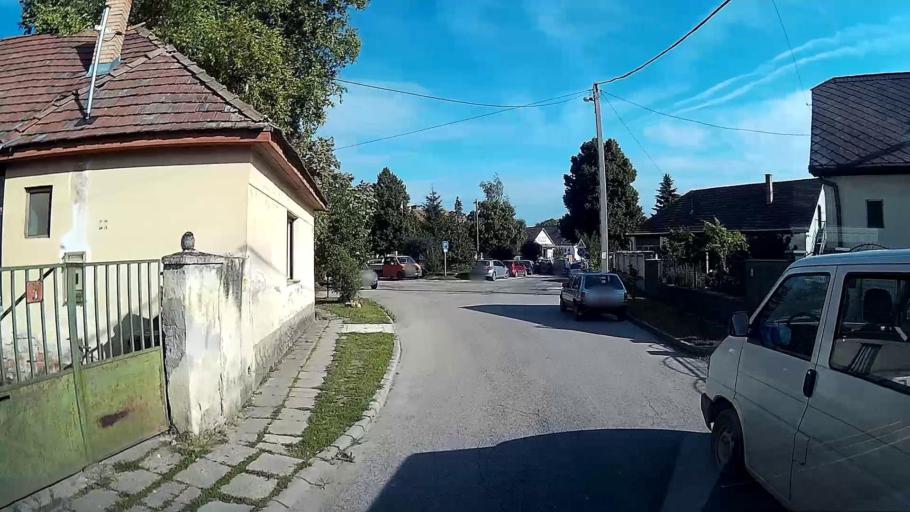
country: HU
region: Pest
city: Szentendre
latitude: 47.6881
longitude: 19.1015
